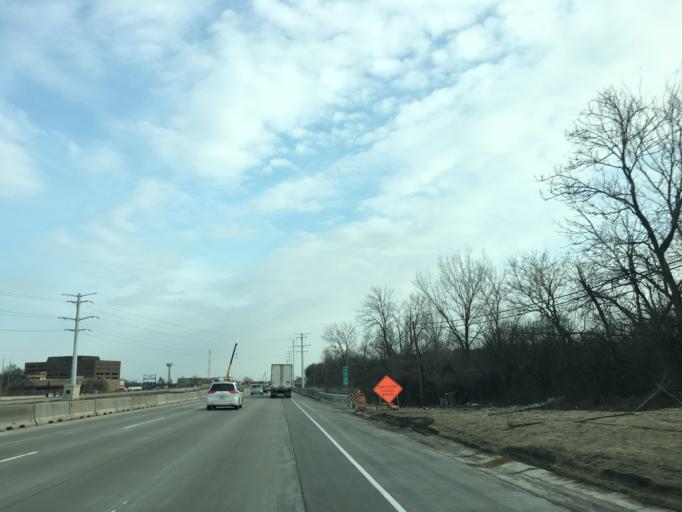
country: US
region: Illinois
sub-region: Cook County
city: Rolling Meadows
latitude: 42.0451
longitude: -87.9940
